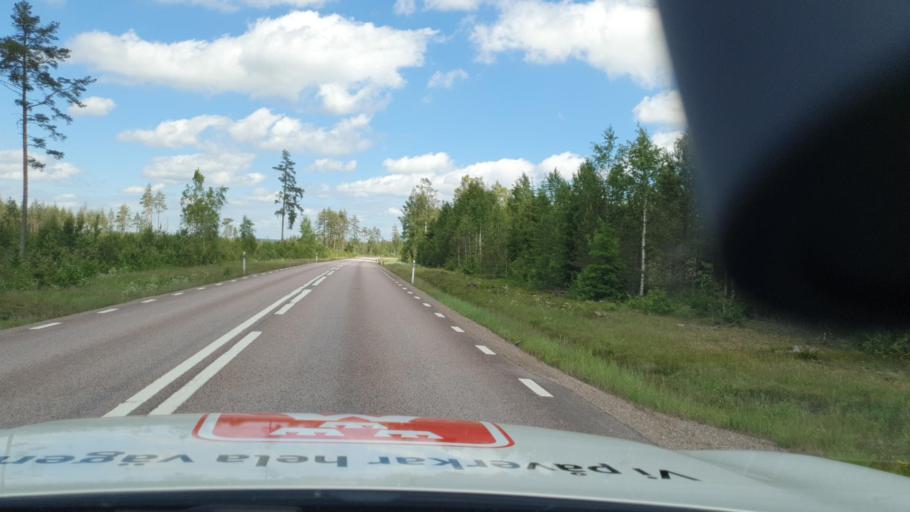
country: SE
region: Vaermland
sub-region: Filipstads Kommun
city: Filipstad
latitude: 59.6515
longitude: 13.9941
